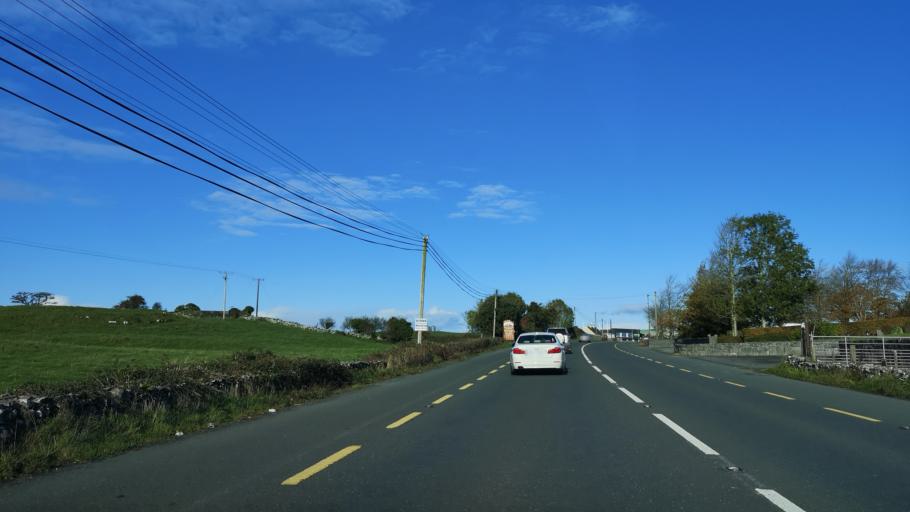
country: IE
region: Connaught
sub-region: County Galway
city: Moycullen
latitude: 53.4598
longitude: -9.1024
